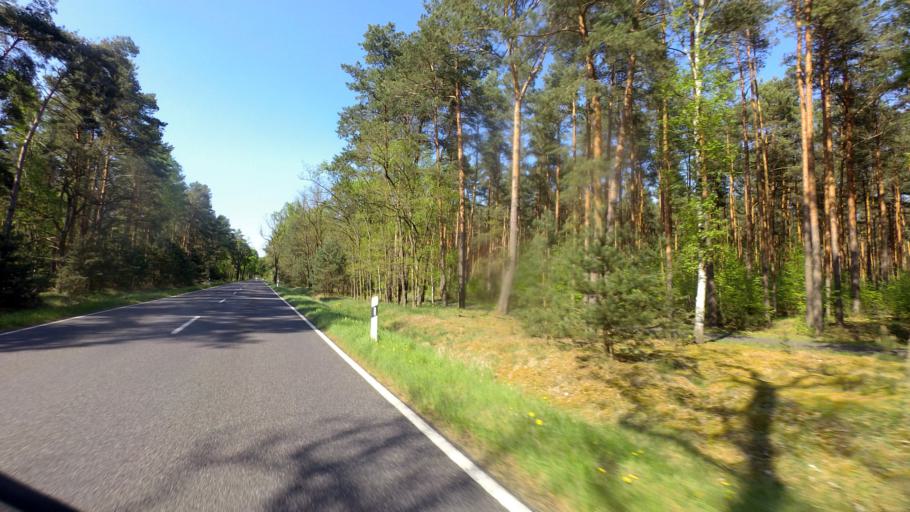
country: DE
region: Brandenburg
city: Halbe
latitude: 52.1426
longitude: 13.7479
